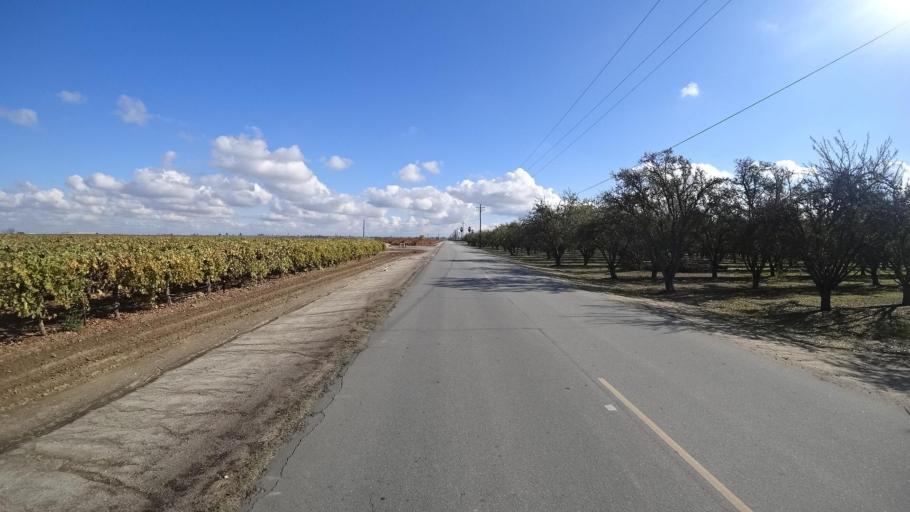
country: US
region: California
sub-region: Kern County
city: McFarland
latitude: 35.6744
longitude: -119.2553
